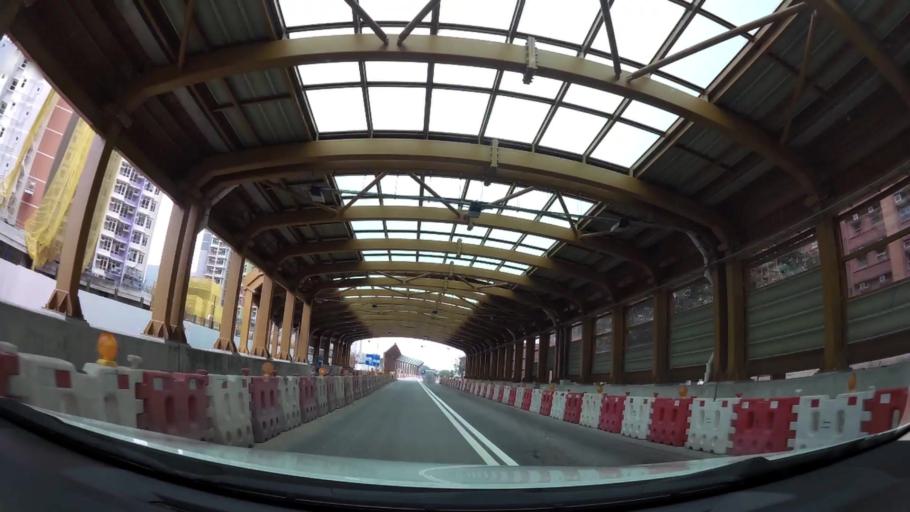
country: HK
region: Tuen Mun
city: Tuen Mun
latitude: 22.4141
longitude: 113.9772
